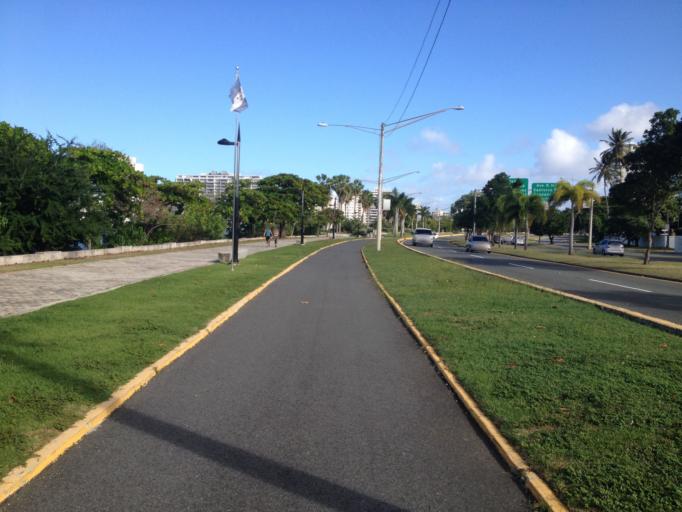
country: PR
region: San Juan
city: San Juan
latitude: 18.4572
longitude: -66.0816
